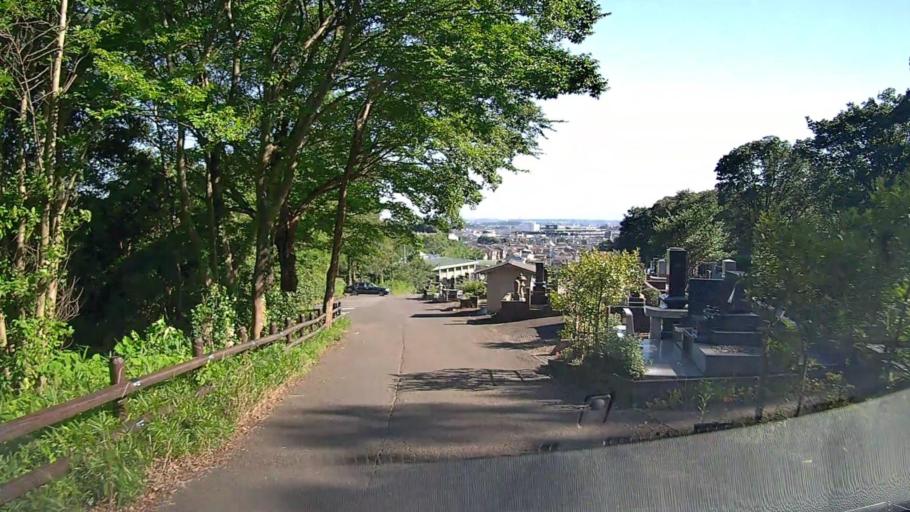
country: JP
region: Tokyo
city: Fussa
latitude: 35.7737
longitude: 139.3619
